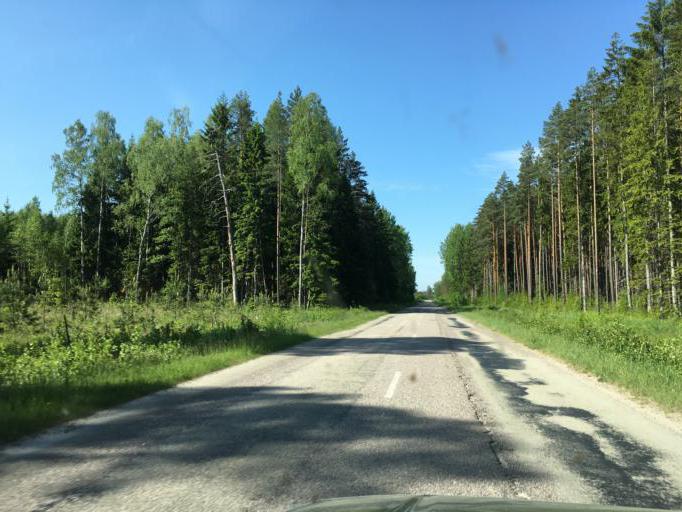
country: LV
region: Ventspils
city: Ventspils
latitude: 57.4875
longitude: 21.7823
